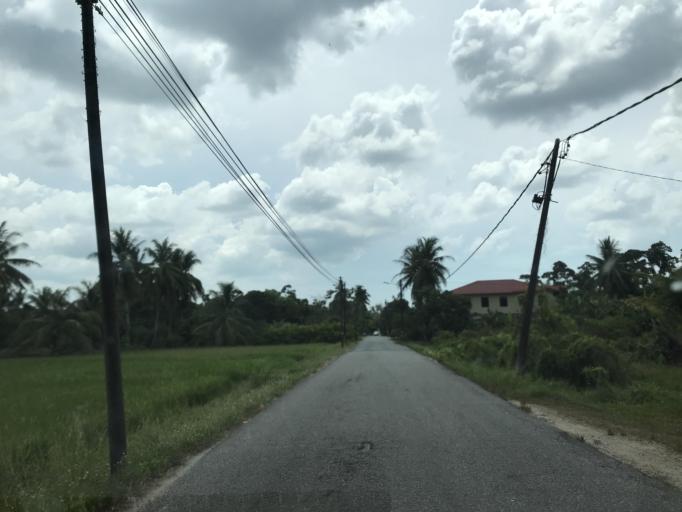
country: MY
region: Kelantan
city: Kota Bharu
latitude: 6.1322
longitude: 102.1811
